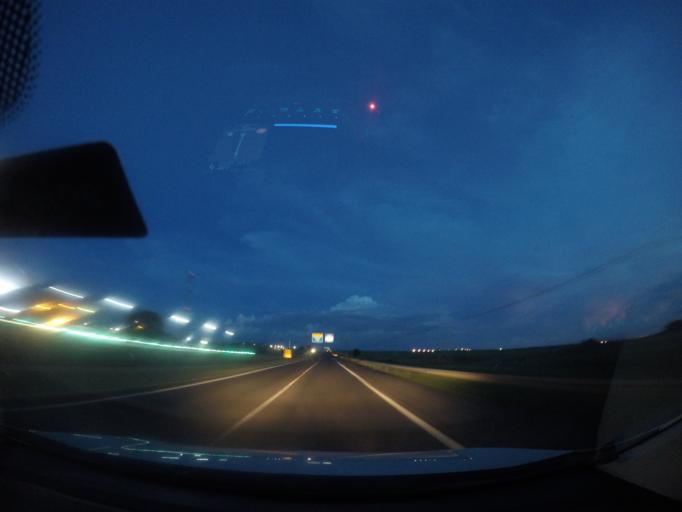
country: BR
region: Sao Paulo
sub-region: Cordeiropolis
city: Cordeiropolis
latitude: -22.4992
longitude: -47.4111
